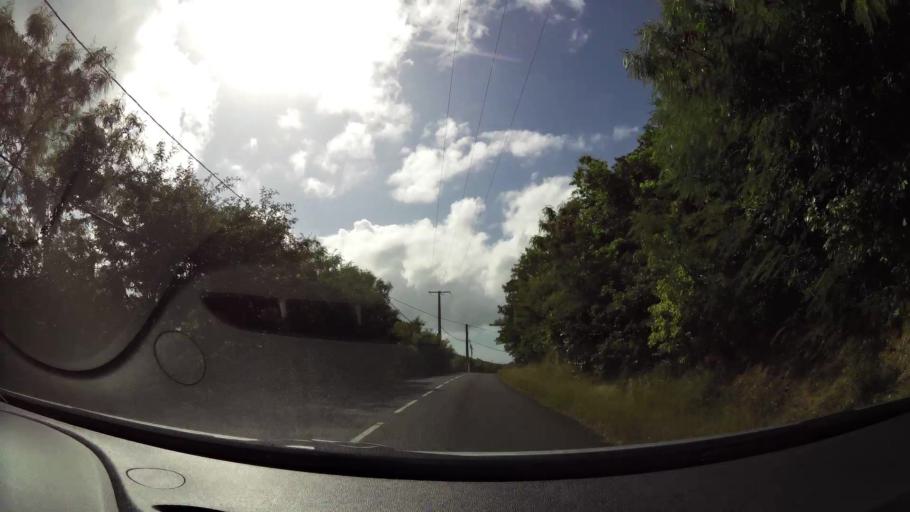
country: MQ
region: Martinique
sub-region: Martinique
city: Le Marin
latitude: 14.4255
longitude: -60.8749
